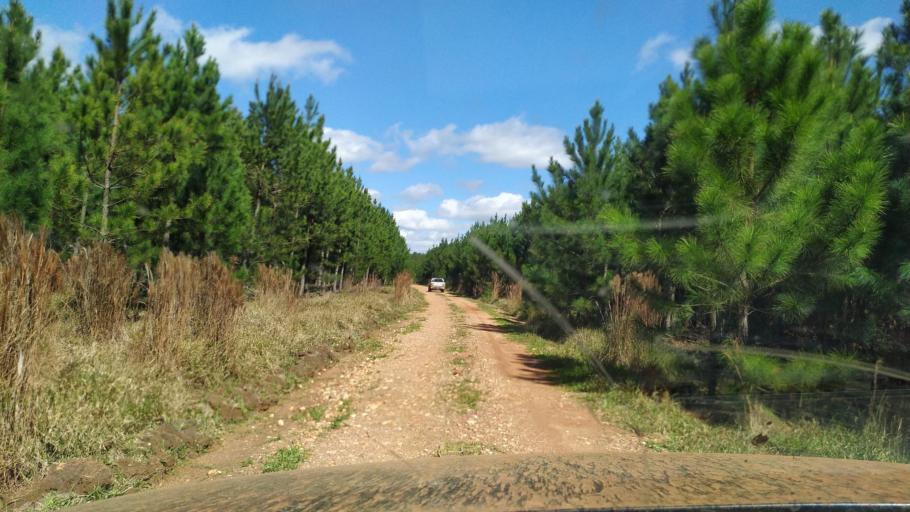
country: AR
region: Corrientes
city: Santo Tome
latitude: -28.4607
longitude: -55.9870
